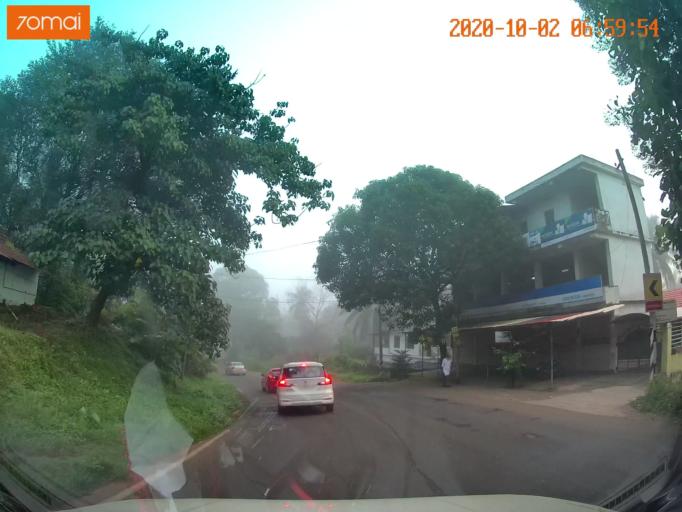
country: IN
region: Kerala
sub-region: Malappuram
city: Tirur
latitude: 10.8780
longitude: 76.0682
